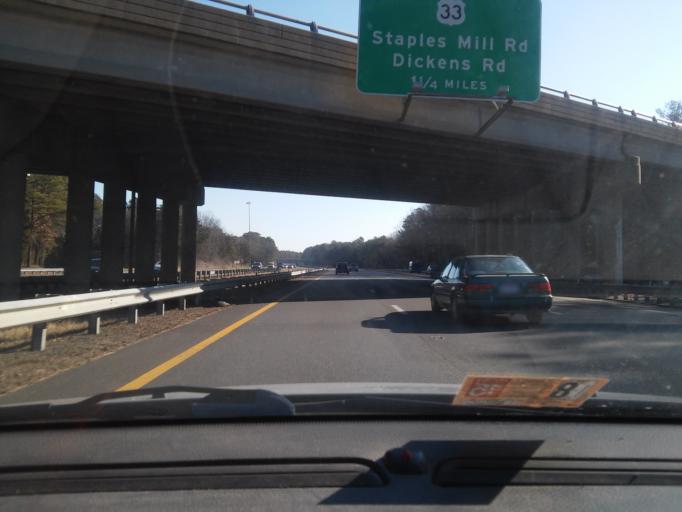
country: US
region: Virginia
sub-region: Henrico County
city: Dumbarton
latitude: 37.6056
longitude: -77.5166
